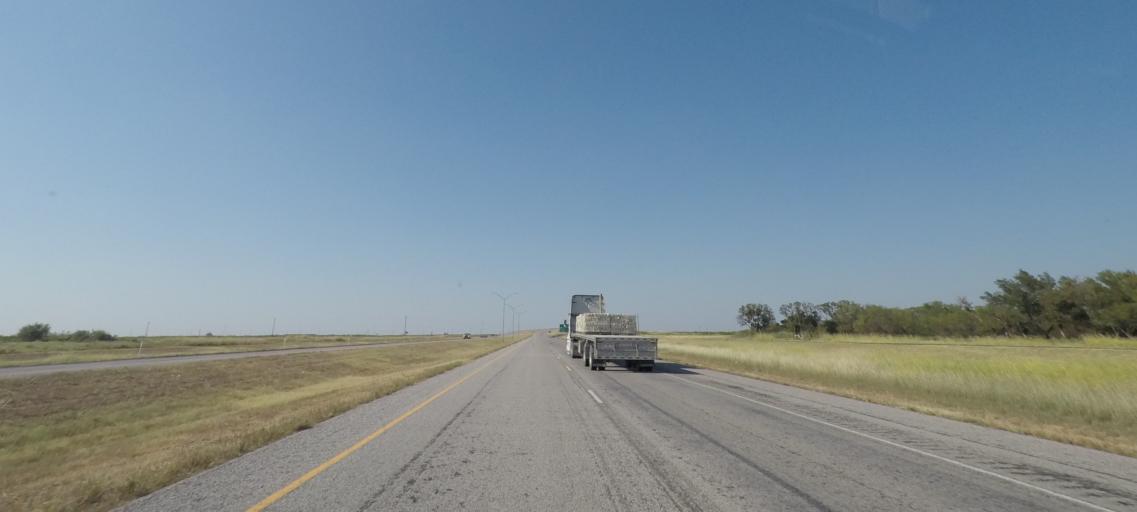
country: US
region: Texas
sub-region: Baylor County
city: Seymour
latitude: 33.6071
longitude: -99.2425
